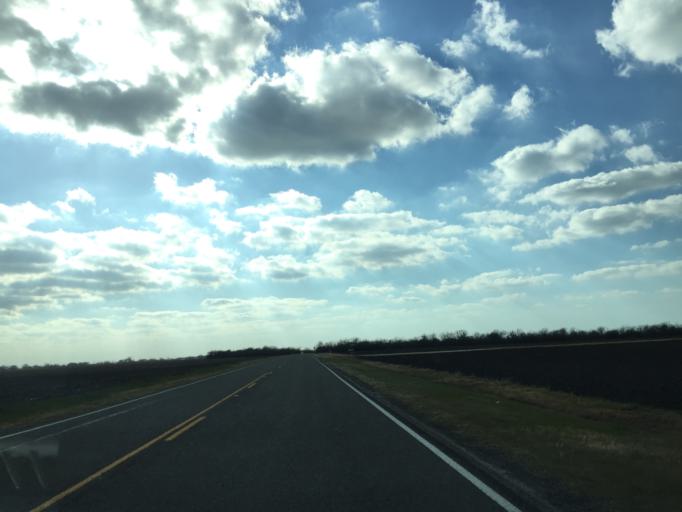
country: US
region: Texas
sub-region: Williamson County
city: Taylor
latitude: 30.6401
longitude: -97.4126
